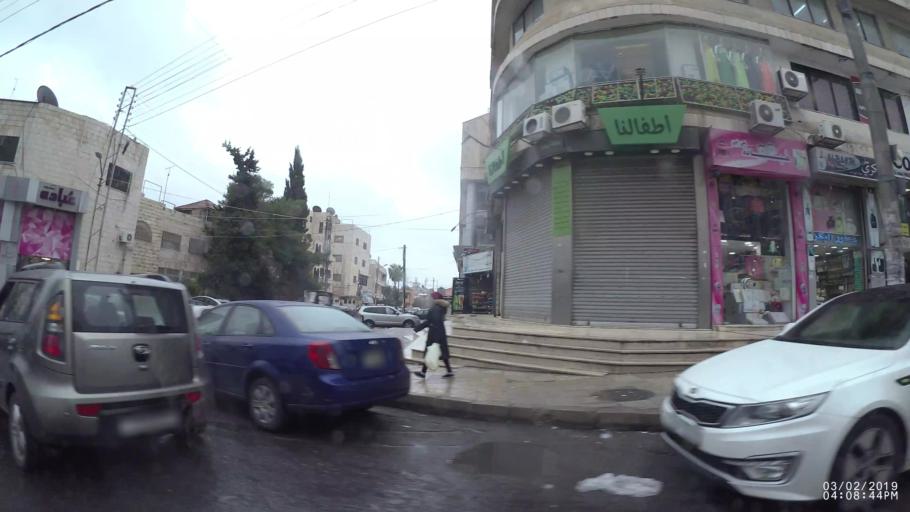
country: JO
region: Amman
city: Amman
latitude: 31.9660
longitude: 35.9200
